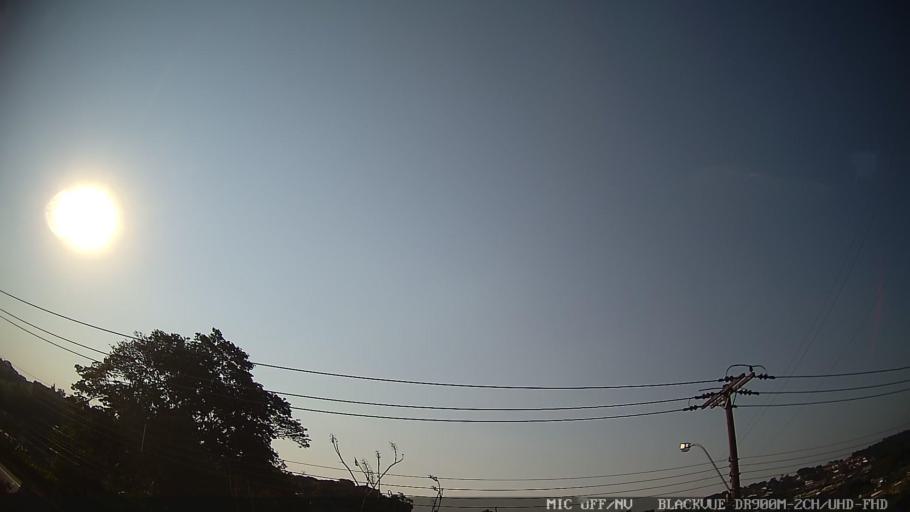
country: BR
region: Sao Paulo
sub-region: Itatiba
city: Itatiba
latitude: -22.9926
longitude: -46.8468
